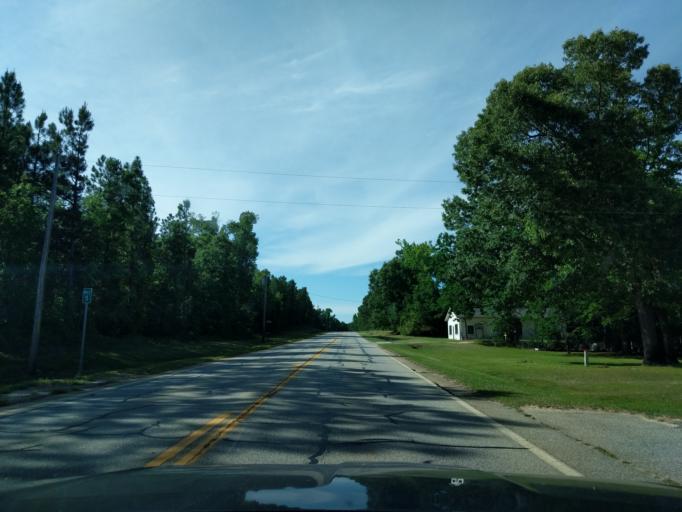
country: US
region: Georgia
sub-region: Jefferson County
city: Wrens
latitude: 33.2409
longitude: -82.3852
